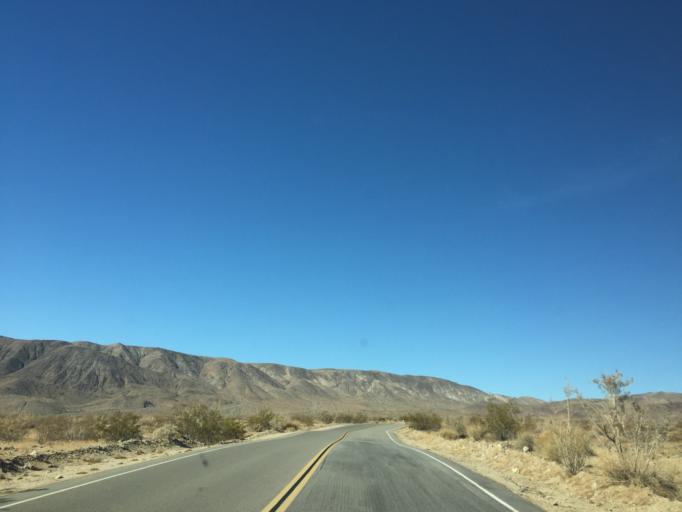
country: US
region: California
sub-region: San Bernardino County
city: Twentynine Palms
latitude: 33.9250
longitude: -115.9162
